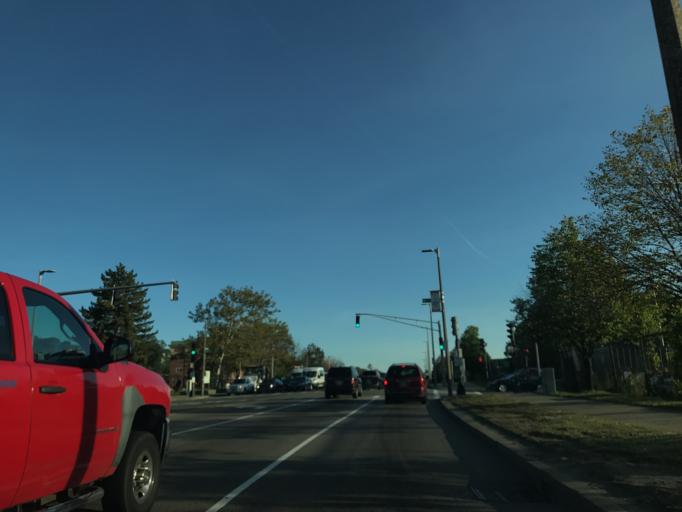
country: US
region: Massachusetts
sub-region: Norfolk County
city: Brookline
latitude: 42.3243
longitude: -71.0984
